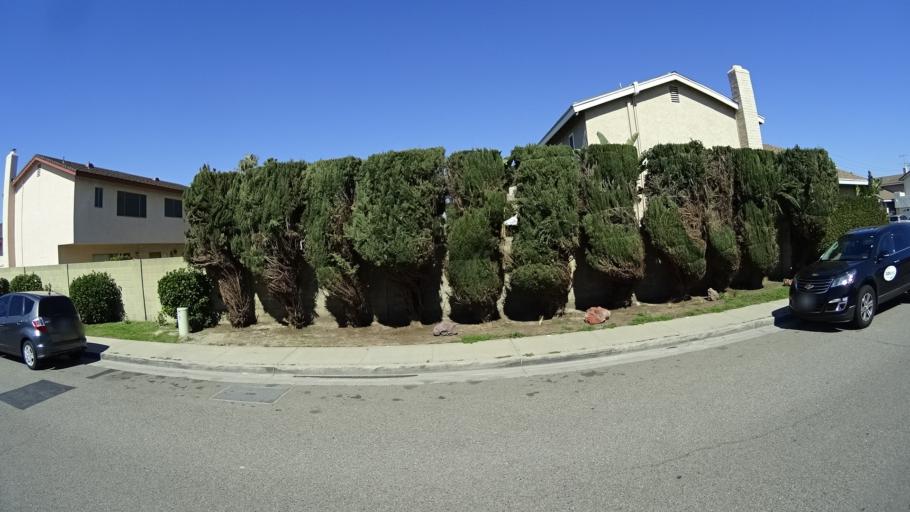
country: US
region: California
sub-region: Orange County
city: Garden Grove
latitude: 33.8054
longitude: -117.9396
